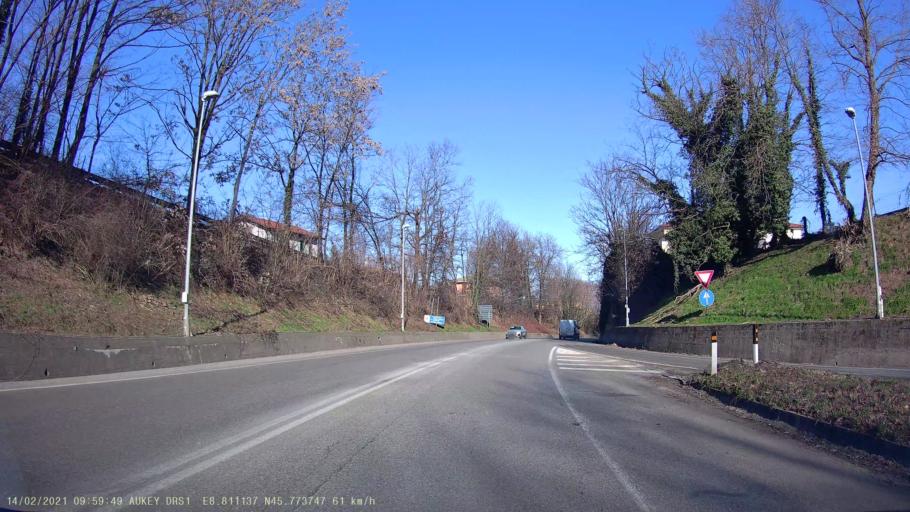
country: IT
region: Lombardy
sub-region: Provincia di Varese
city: Buguggiate
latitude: 45.7740
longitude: 8.8109
